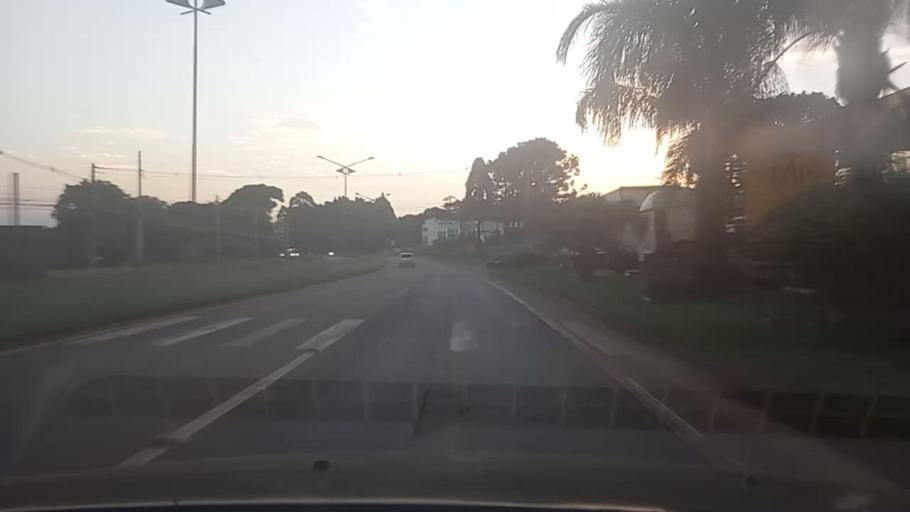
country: BR
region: Rio Grande do Sul
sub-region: Passo Fundo
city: Passo Fundo
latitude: -28.2738
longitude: -52.4461
